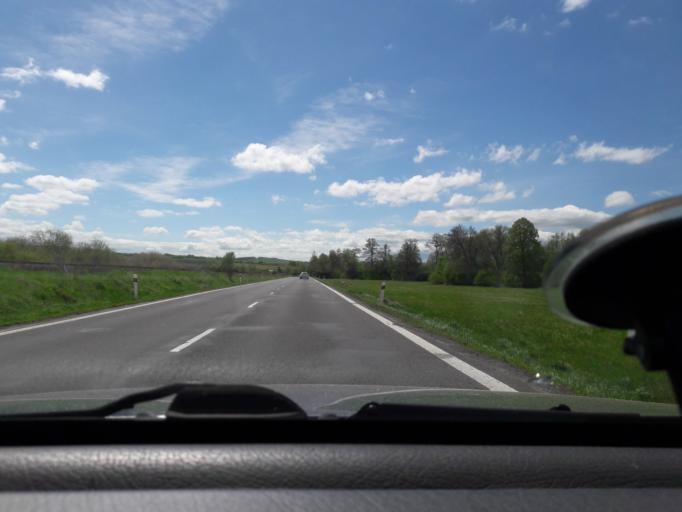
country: SK
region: Banskobystricky
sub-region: Okres Banska Bystrica
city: Zvolen
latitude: 48.4916
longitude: 19.0990
